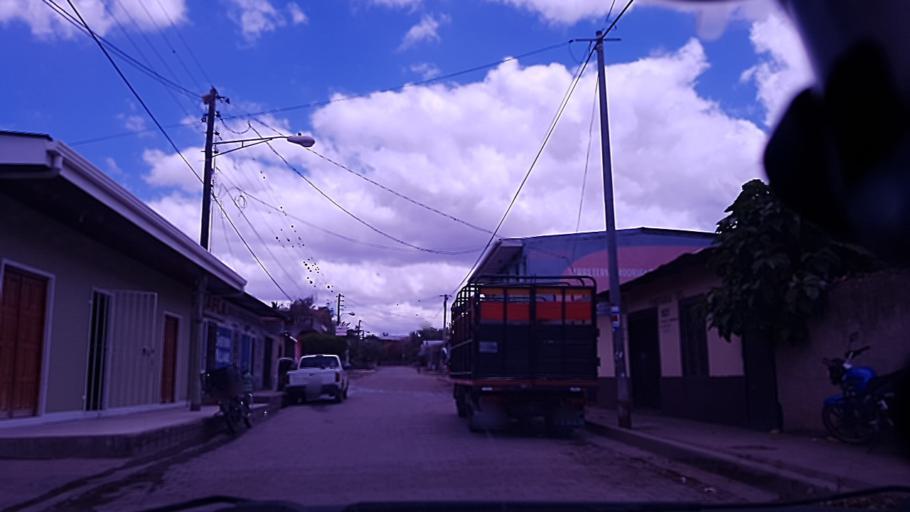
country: NI
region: Esteli
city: Condega
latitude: 13.3655
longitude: -86.3983
